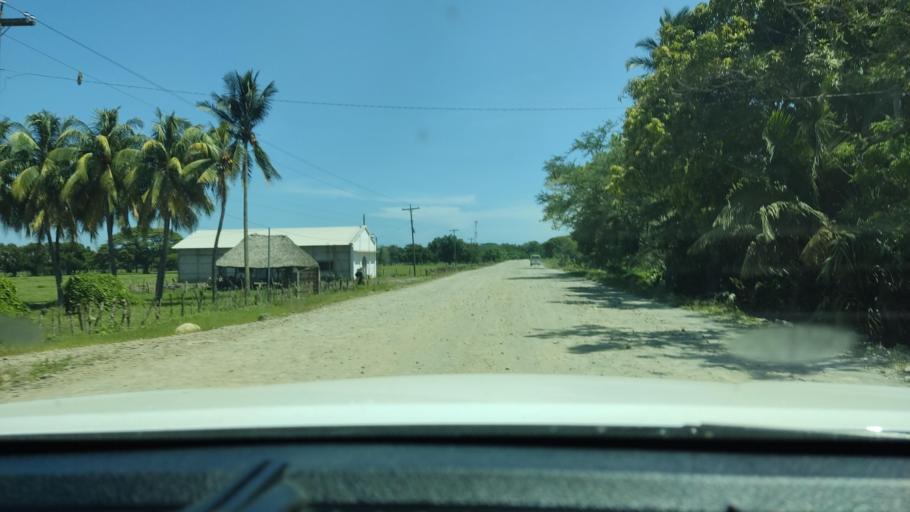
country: SV
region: Ahuachapan
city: San Francisco Menendez
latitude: 13.7606
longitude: -90.1177
